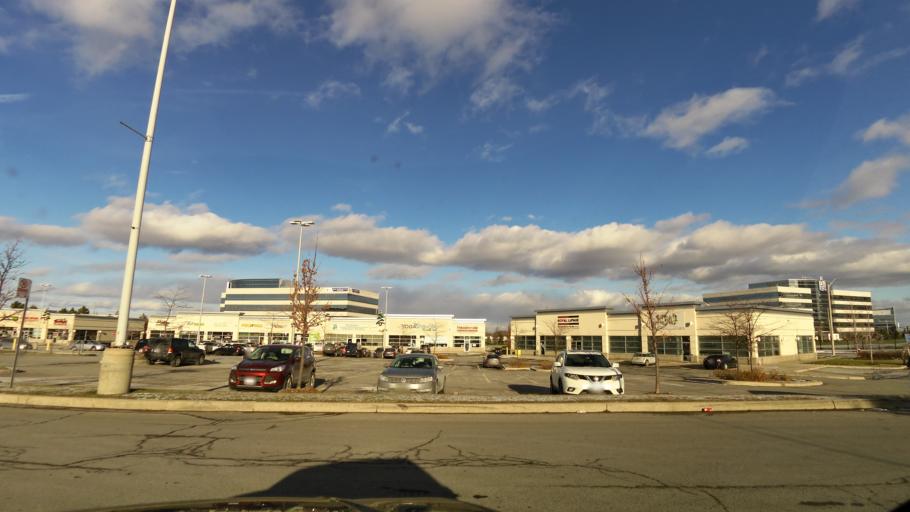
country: CA
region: Ontario
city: Brampton
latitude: 43.6096
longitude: -79.7491
